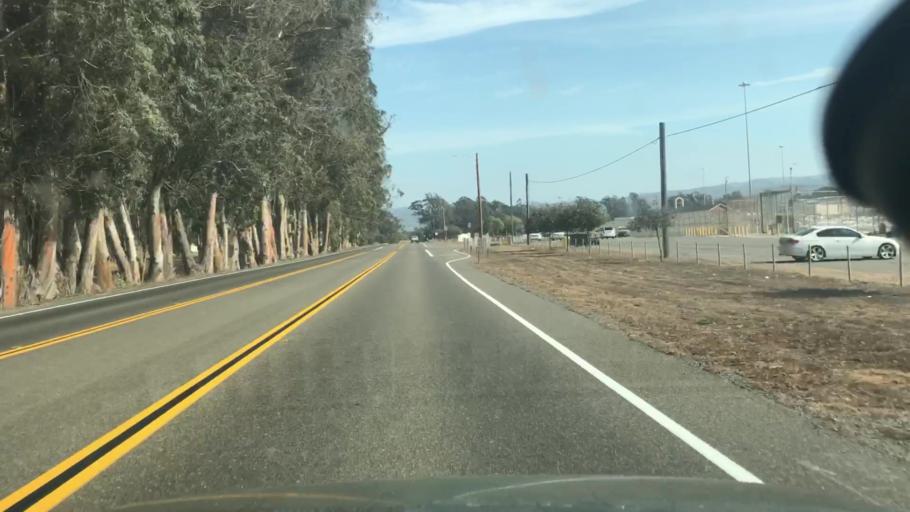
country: US
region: California
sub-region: Santa Barbara County
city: Vandenberg Village
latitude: 34.6802
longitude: -120.4988
